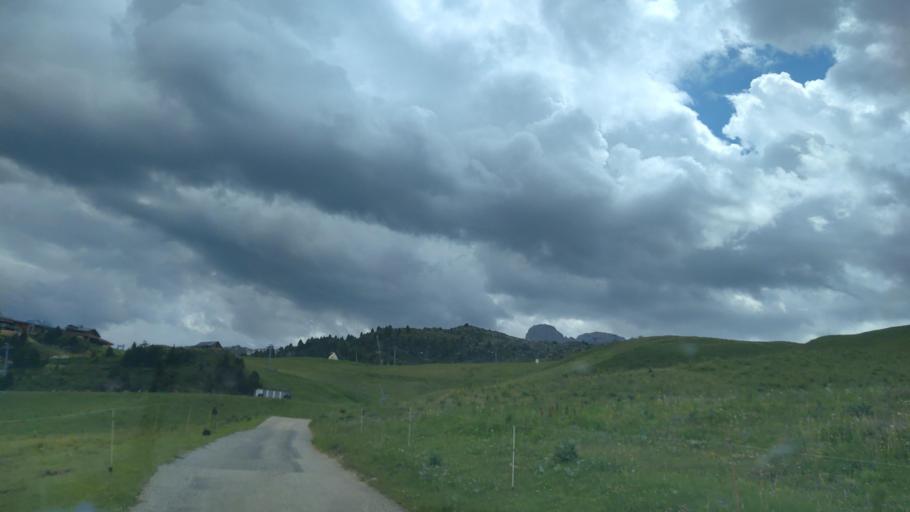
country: FR
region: Rhone-Alpes
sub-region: Departement de la Savoie
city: Courchevel
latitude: 45.3953
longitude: 6.6501
